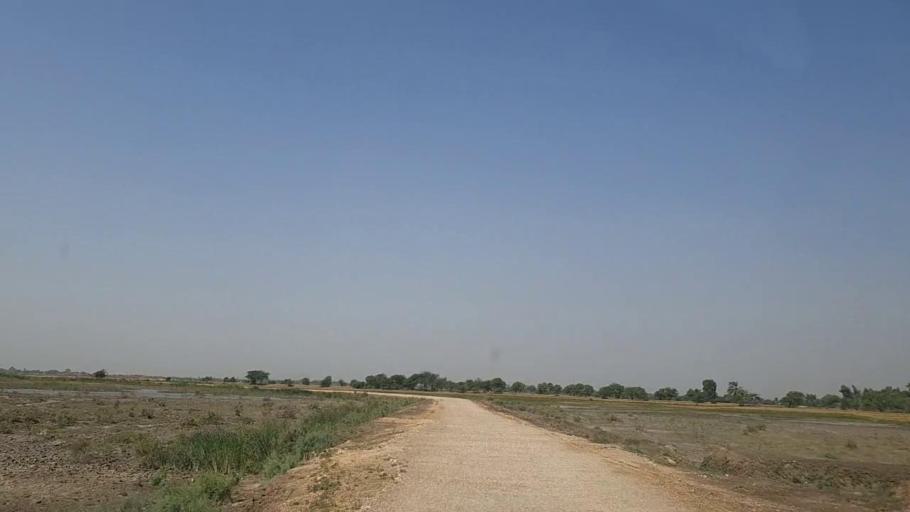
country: PK
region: Sindh
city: Daro Mehar
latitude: 24.7528
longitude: 68.1394
